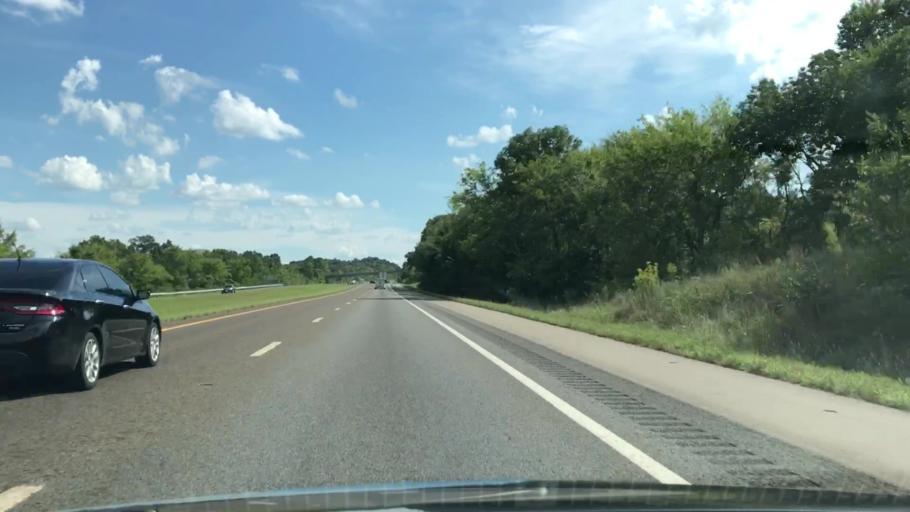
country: US
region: Tennessee
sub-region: Marshall County
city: Lewisburg
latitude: 35.5021
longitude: -86.8929
